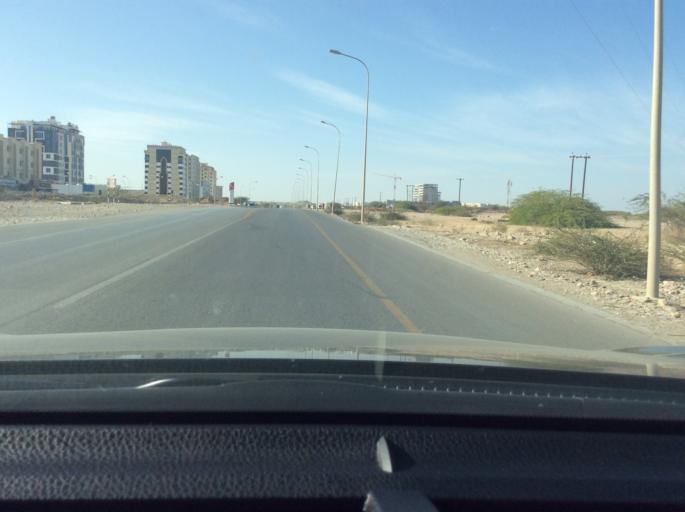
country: OM
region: Muhafazat Masqat
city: As Sib al Jadidah
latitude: 23.5741
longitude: 58.1858
